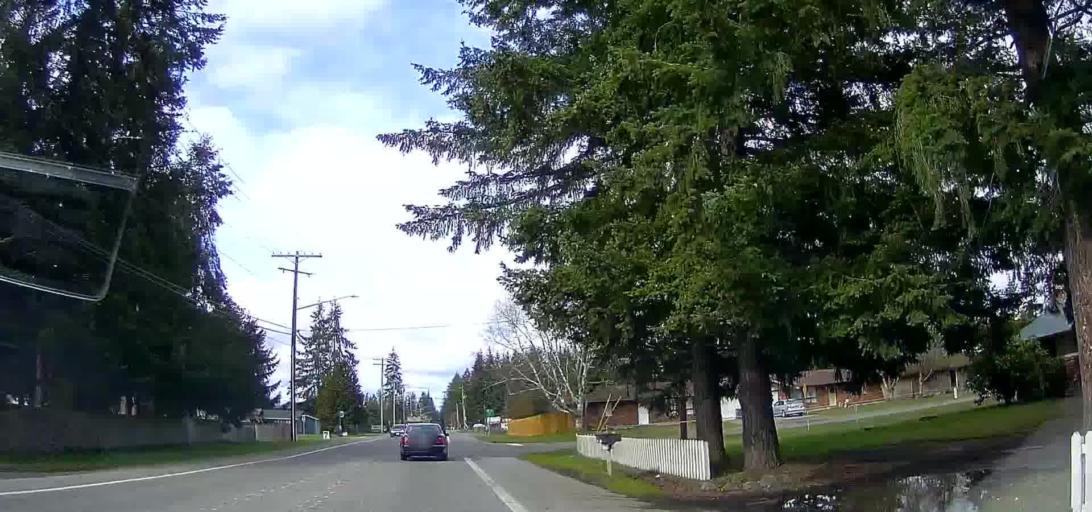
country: US
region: Washington
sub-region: Snohomish County
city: Smokey Point
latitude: 48.1564
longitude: -122.1829
